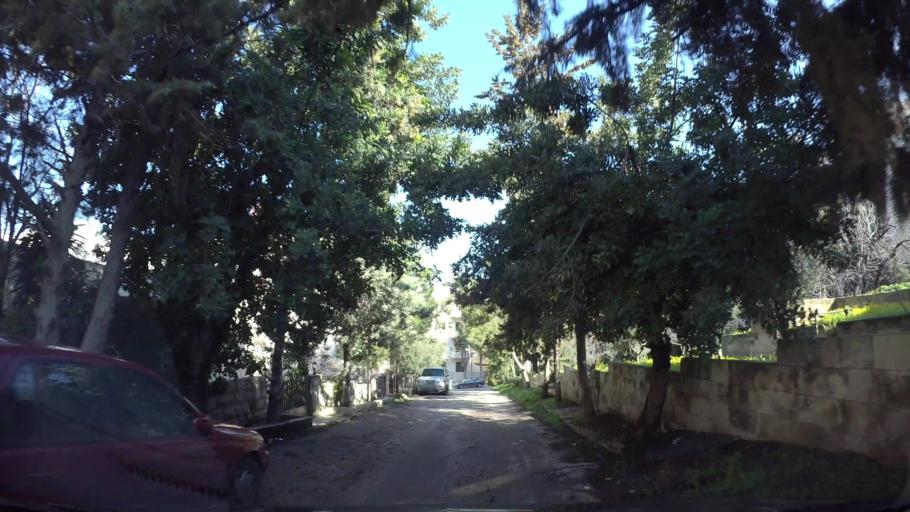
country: JO
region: Amman
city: Al Jubayhah
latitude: 32.0006
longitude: 35.8789
